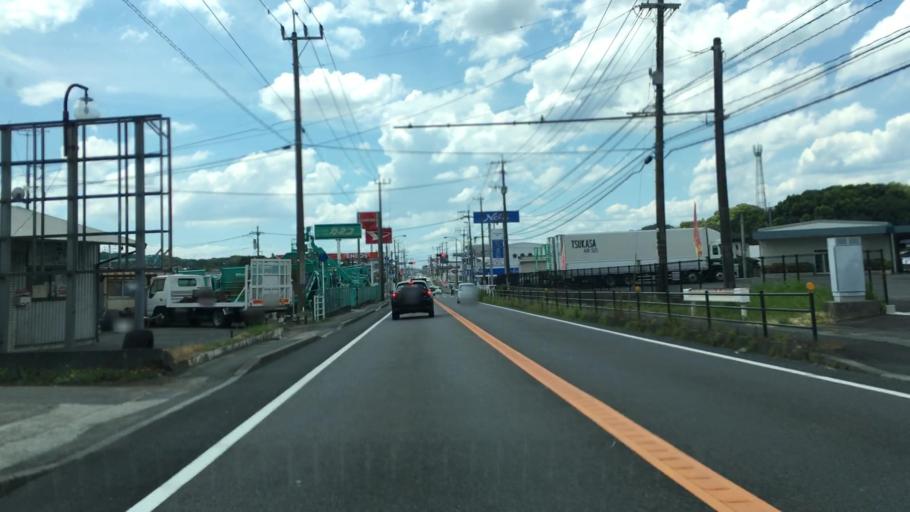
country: JP
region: Saga Prefecture
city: Tosu
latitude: 33.3578
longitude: 130.4889
